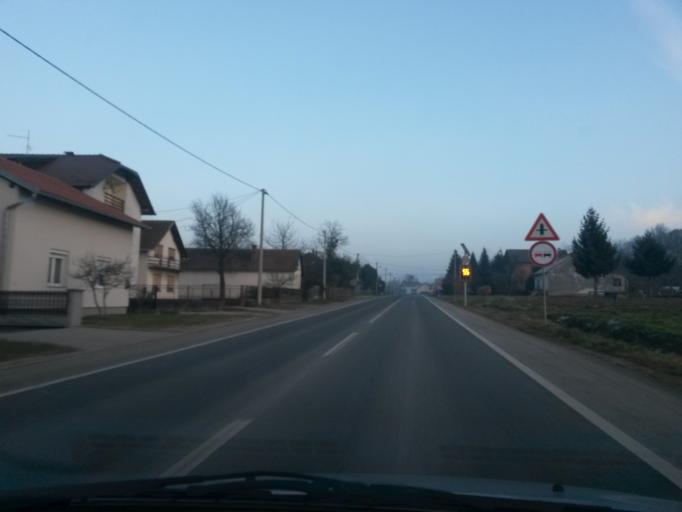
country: HR
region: Varazdinska
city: Ludbreg
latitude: 46.2384
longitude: 16.6369
